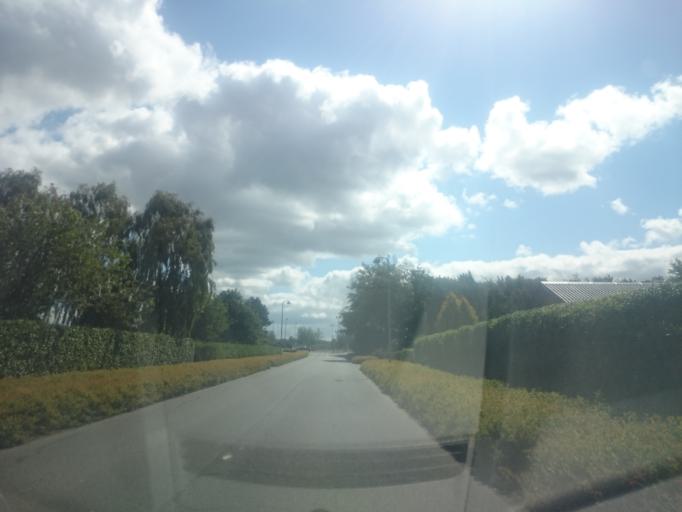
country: DK
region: South Denmark
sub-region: Billund Kommune
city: Billund
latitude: 55.7242
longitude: 9.1123
